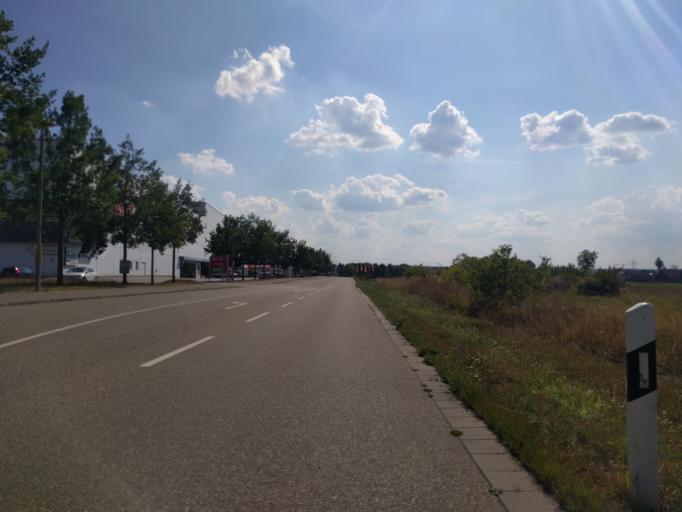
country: DE
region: Bavaria
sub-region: Upper Palatinate
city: Tegernheim
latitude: 49.0055
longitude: 12.1769
